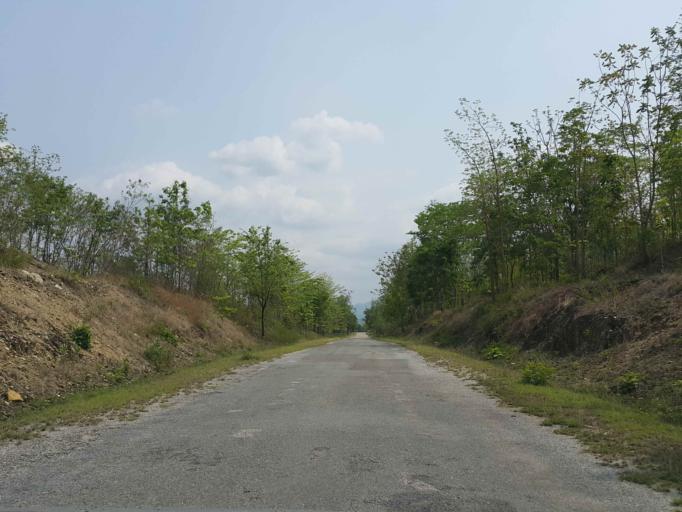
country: TH
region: Sukhothai
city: Thung Saliam
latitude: 17.3324
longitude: 99.4239
